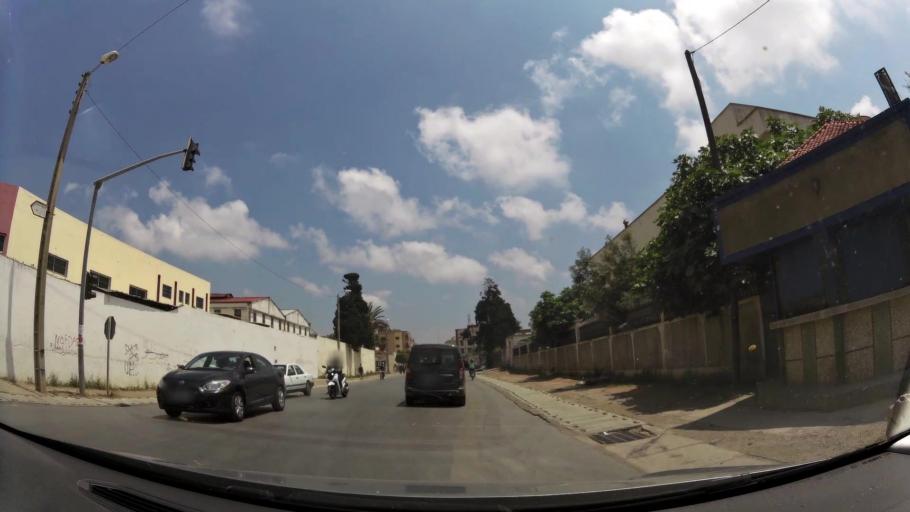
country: MA
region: Rabat-Sale-Zemmour-Zaer
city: Sale
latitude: 34.0603
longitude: -6.7915
